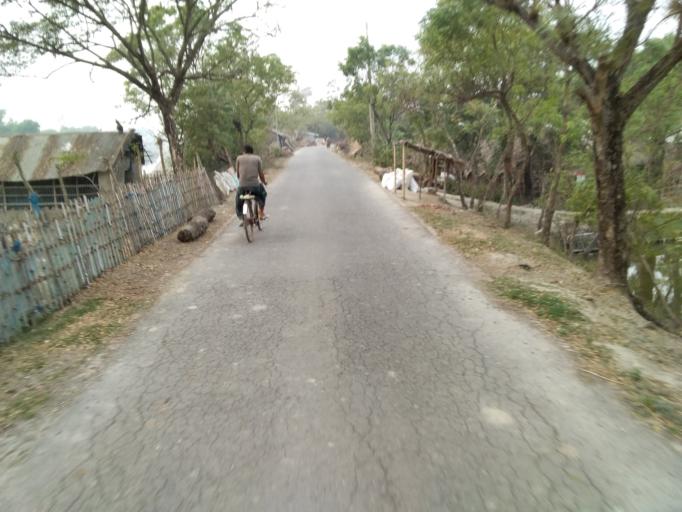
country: BD
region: Khulna
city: Satkhira
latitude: 22.5767
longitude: 89.0737
